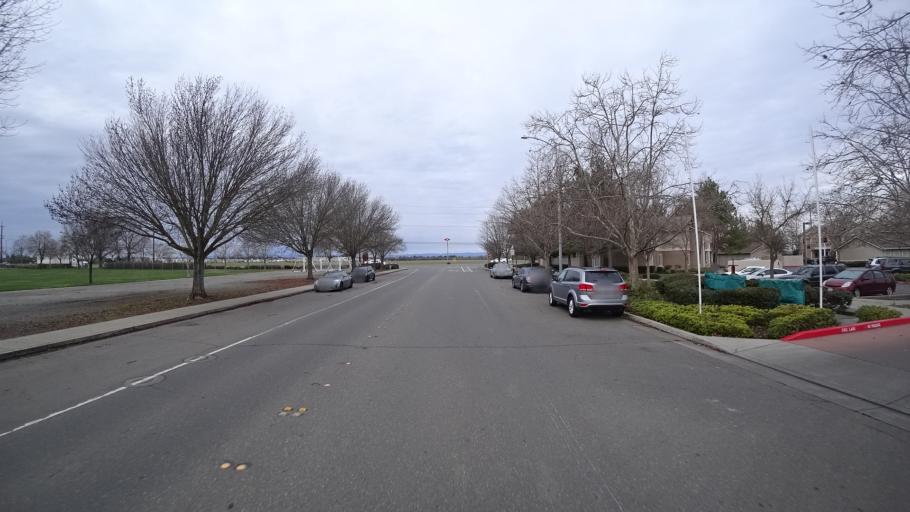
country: US
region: California
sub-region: Yolo County
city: Davis
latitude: 38.5704
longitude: -121.7296
